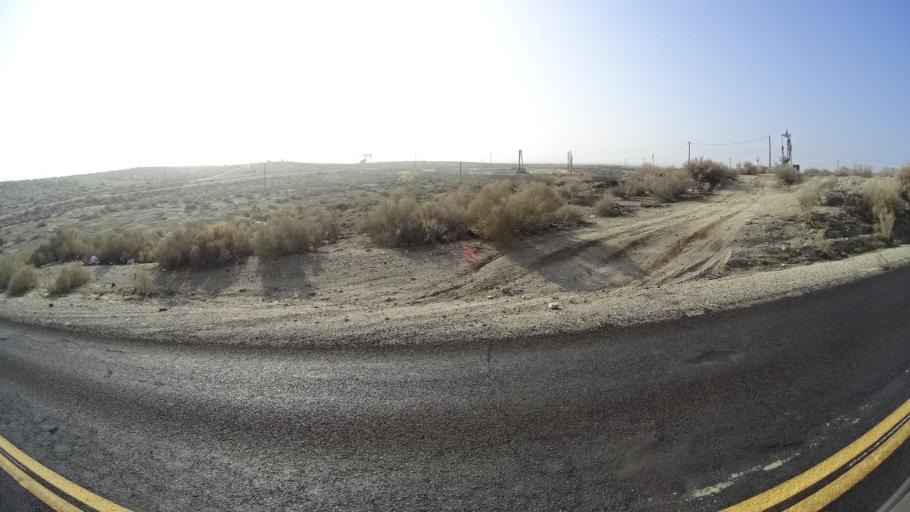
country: US
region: California
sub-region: Kern County
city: Ford City
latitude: 35.1807
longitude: -119.4709
